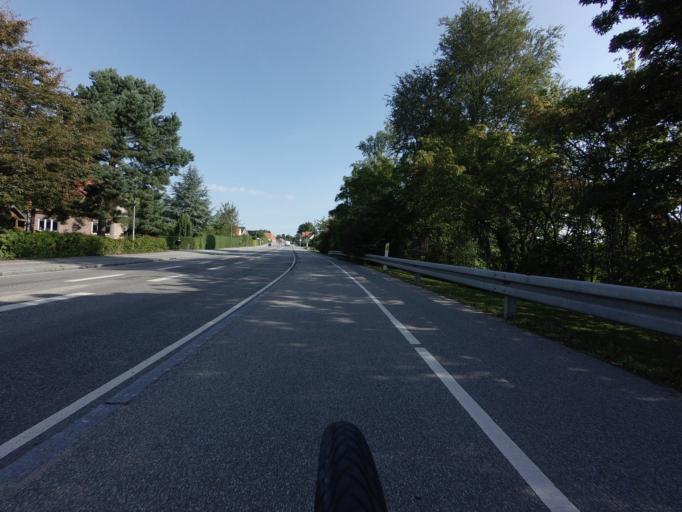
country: DK
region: Zealand
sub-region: Soro Kommune
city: Soro
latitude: 55.4514
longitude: 11.5579
